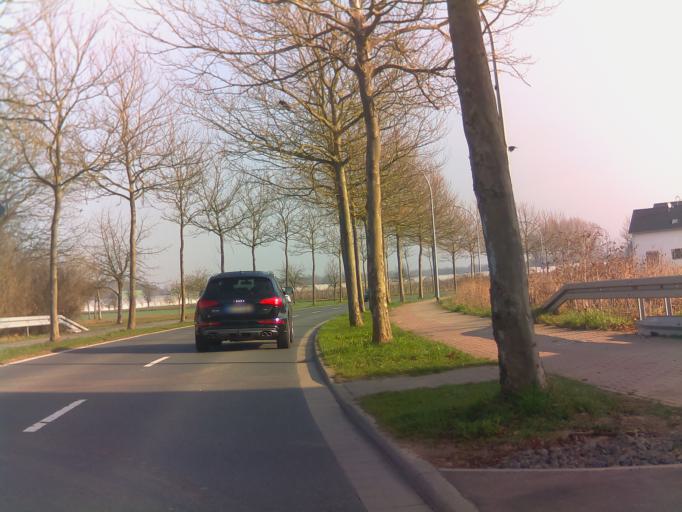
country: DE
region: Hesse
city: Zwingenberg
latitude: 49.7251
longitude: 8.6015
